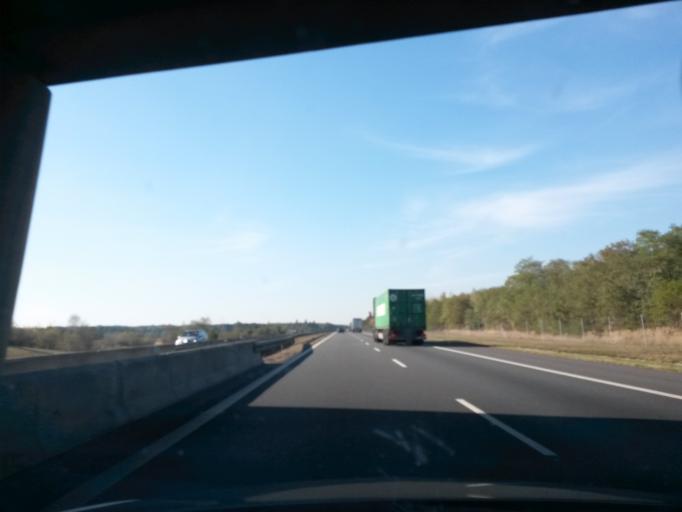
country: PL
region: Opole Voivodeship
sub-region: Powiat opolski
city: Proszkow
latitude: 50.5771
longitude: 17.8434
